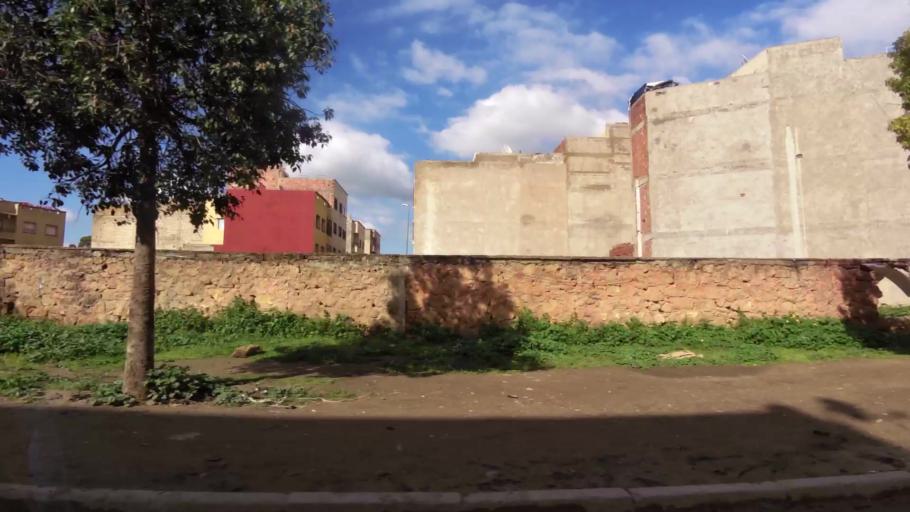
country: MA
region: Chaouia-Ouardigha
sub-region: Settat Province
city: Berrechid
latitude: 33.2740
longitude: -7.5694
